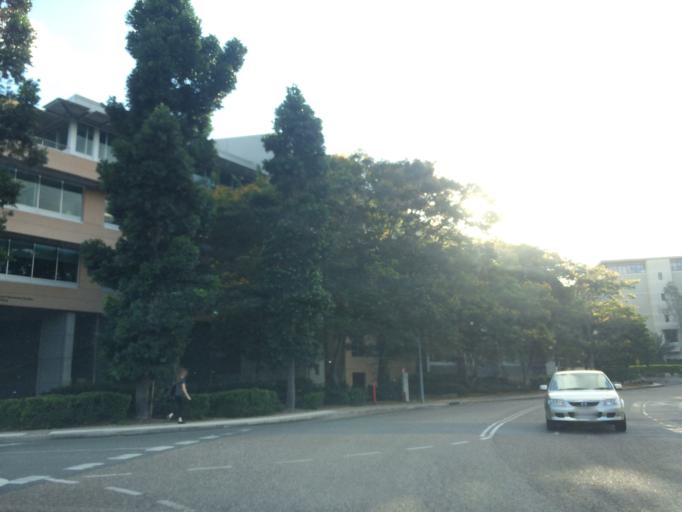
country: AU
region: Queensland
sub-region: Brisbane
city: South Brisbane
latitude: -27.4949
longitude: 153.0162
